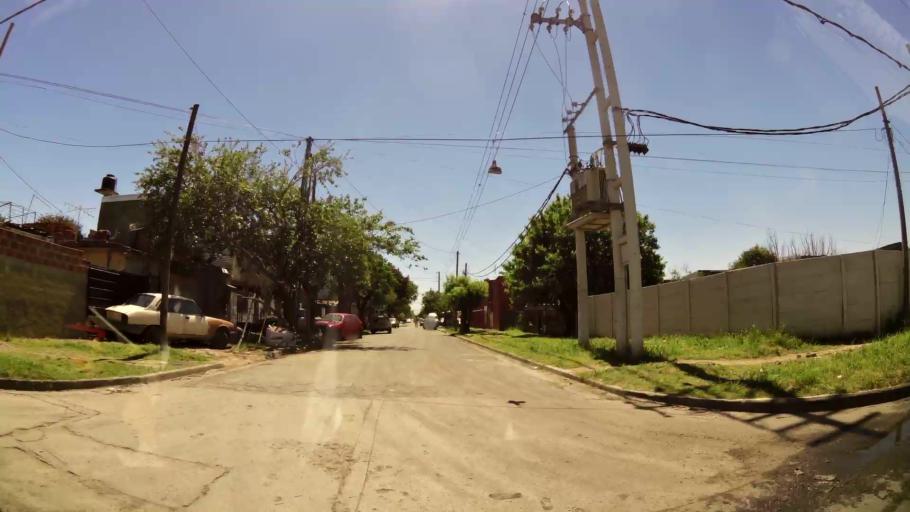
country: AR
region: Buenos Aires
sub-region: Partido de Lanus
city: Lanus
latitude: -34.7328
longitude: -58.3399
